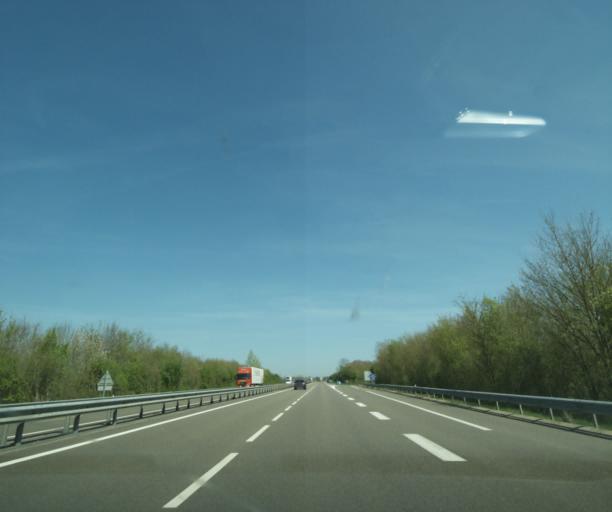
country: FR
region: Bourgogne
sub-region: Departement de la Nievre
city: Saint-Eloi
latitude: 46.9763
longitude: 3.1990
